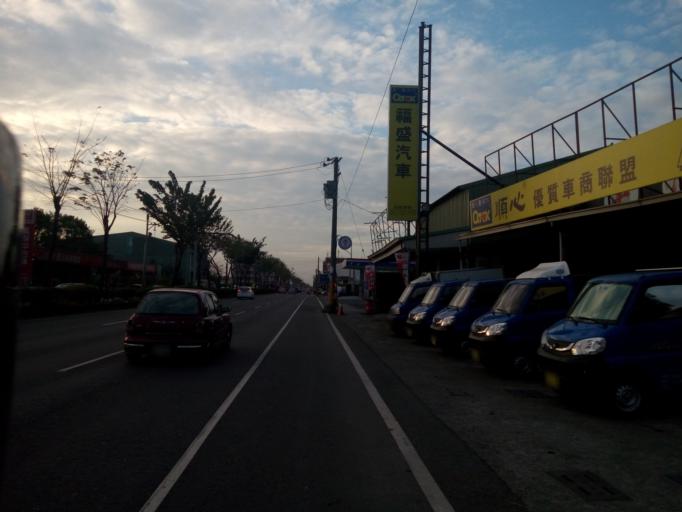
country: TW
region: Taiwan
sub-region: Chiayi
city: Jiayi Shi
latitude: 23.4883
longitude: 120.4106
